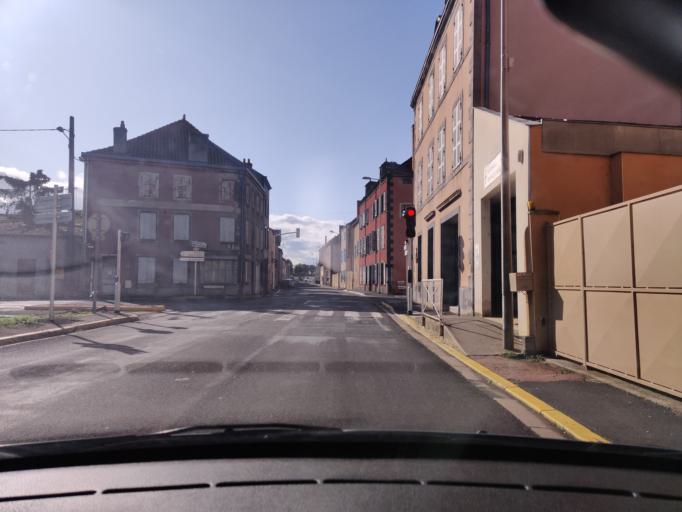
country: FR
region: Auvergne
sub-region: Departement du Puy-de-Dome
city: Aigueperse
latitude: 46.0181
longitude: 3.2008
